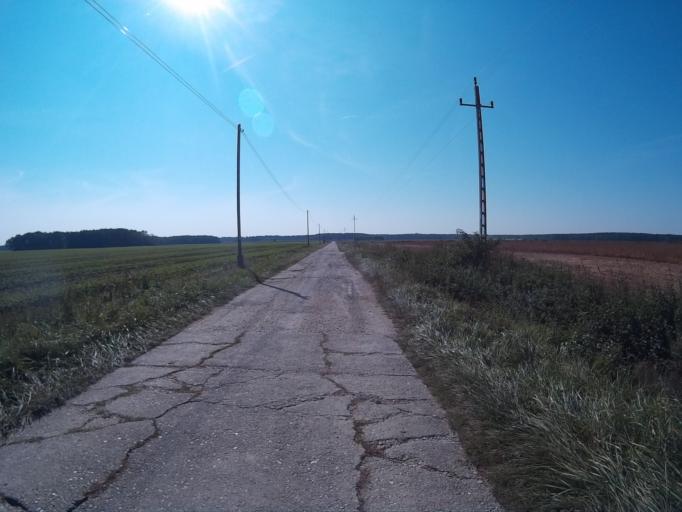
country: HU
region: Vas
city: Kormend
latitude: 47.0815
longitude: 16.6282
